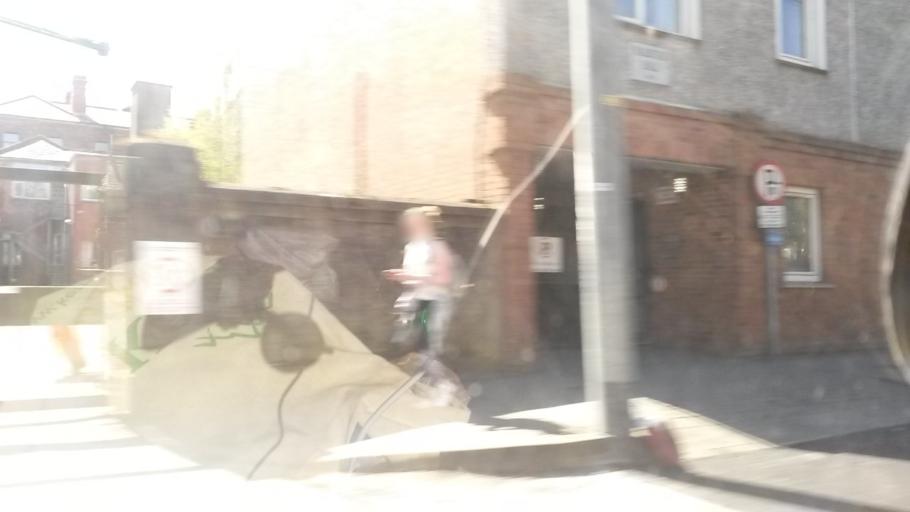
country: IE
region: Munster
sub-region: County Cork
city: Cork
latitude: 51.8968
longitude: -8.4870
